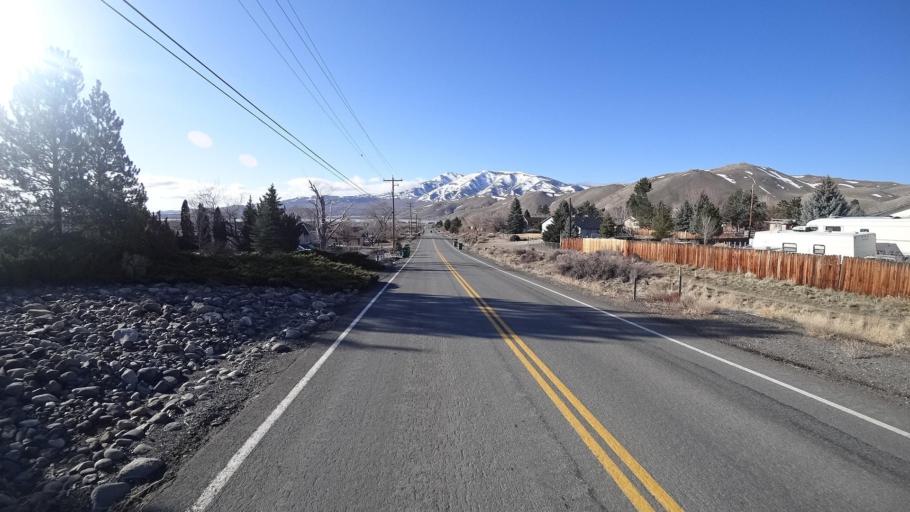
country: US
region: Nevada
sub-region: Washoe County
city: Cold Springs
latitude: 39.6631
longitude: -119.9224
